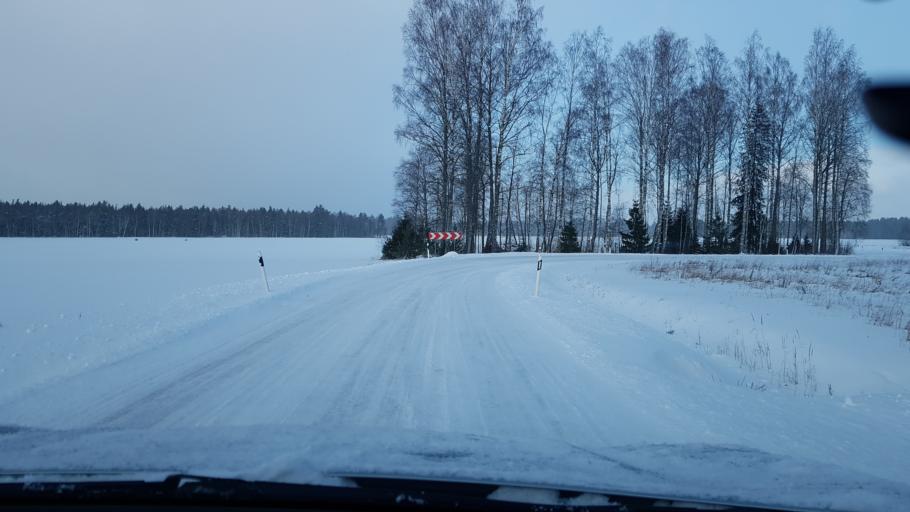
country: EE
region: Harju
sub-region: Nissi vald
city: Turba
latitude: 59.1971
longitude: 24.1388
